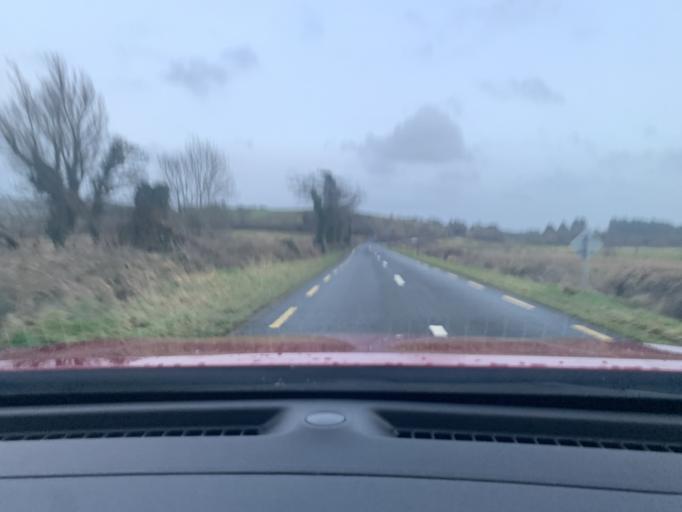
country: IE
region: Connaught
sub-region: Sligo
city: Ballymote
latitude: 54.0392
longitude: -8.4326
